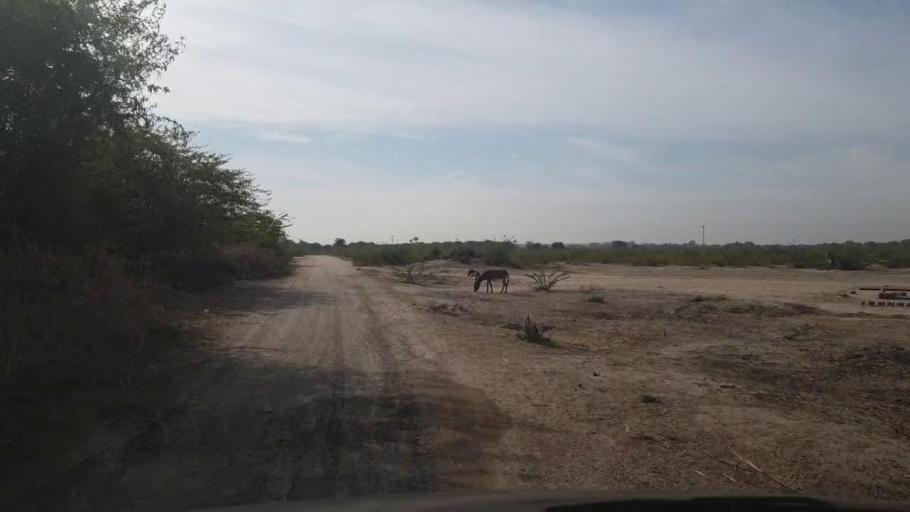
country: PK
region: Sindh
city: Umarkot
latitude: 25.3009
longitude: 69.7179
